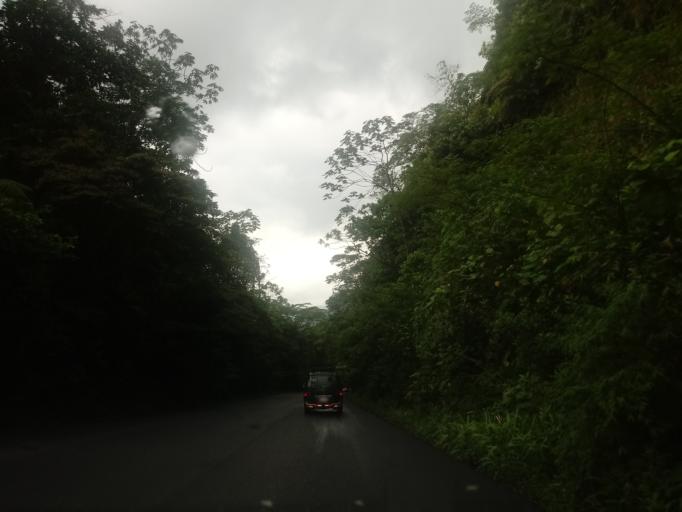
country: CR
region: San Jose
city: Dulce Nombre de Jesus
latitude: 10.1552
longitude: -83.9545
